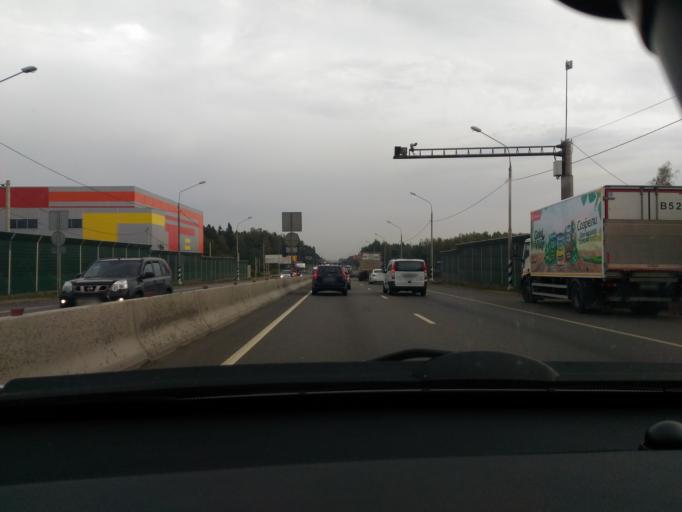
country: RU
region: Moskovskaya
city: Lozhki
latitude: 56.0915
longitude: 37.1108
